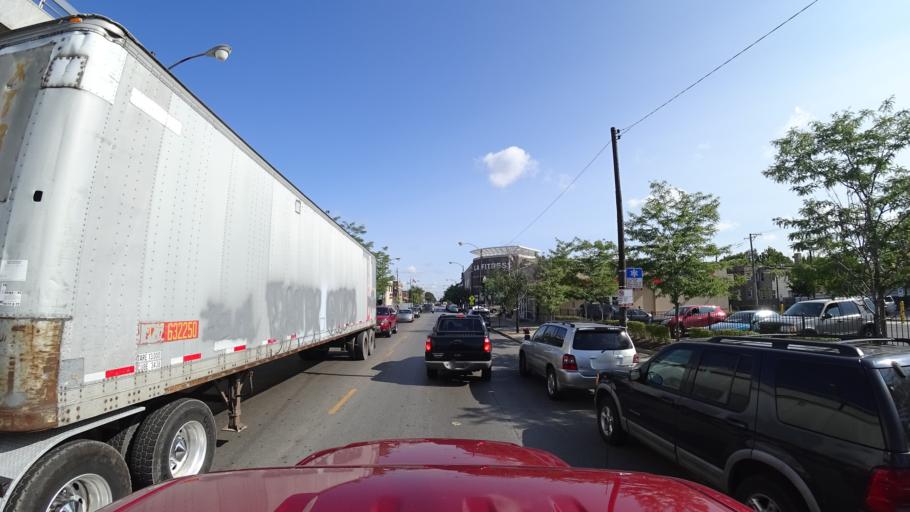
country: US
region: Illinois
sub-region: Cook County
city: Hometown
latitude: 41.7910
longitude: -87.7035
